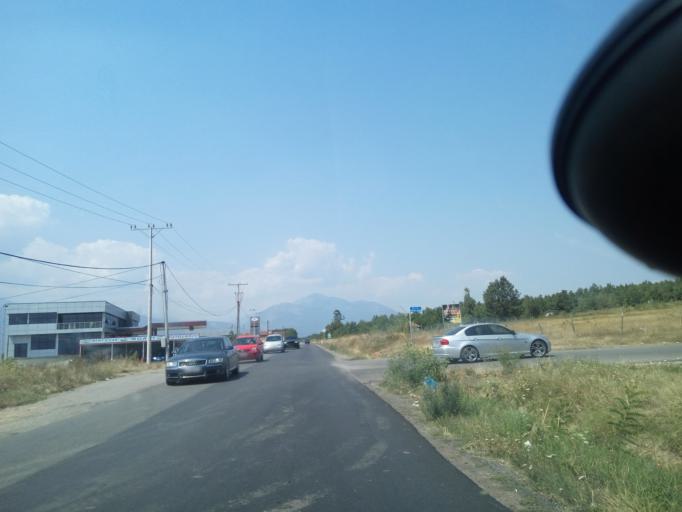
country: XK
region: Gjakova
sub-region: Komuna e Decanit
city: Gllogjan
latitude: 42.4505
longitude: 20.3609
